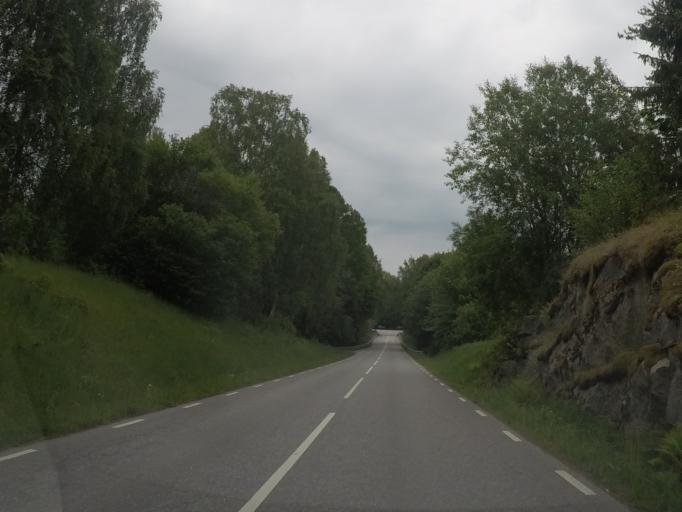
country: SE
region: Soedermanland
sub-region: Nykopings Kommun
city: Svalsta
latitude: 58.8237
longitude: 16.9257
